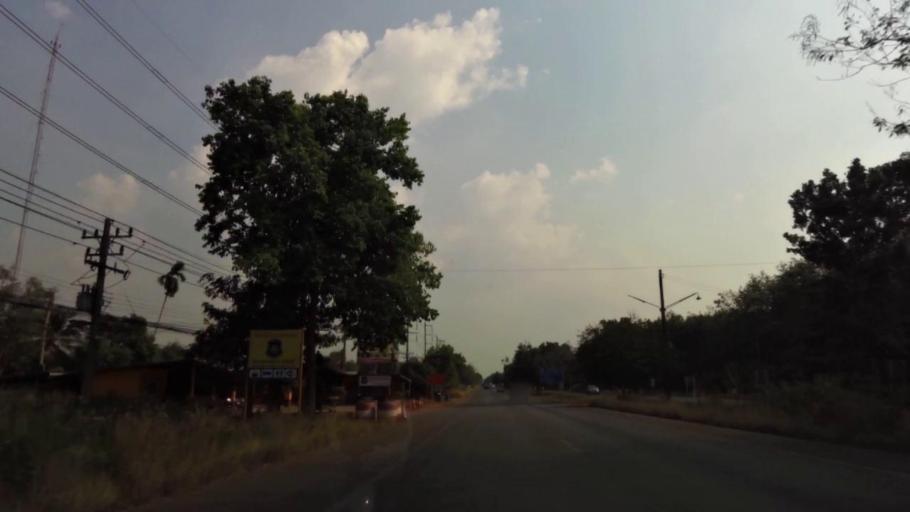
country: TH
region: Rayong
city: Wang Chan
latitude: 12.8980
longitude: 101.5435
